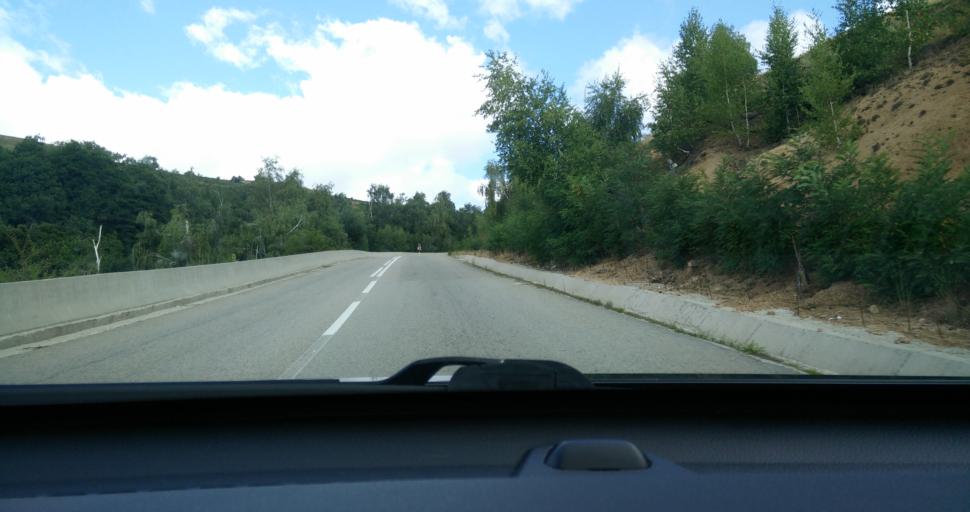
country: RO
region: Gorj
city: Novaci-Straini
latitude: 45.2133
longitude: 23.6980
